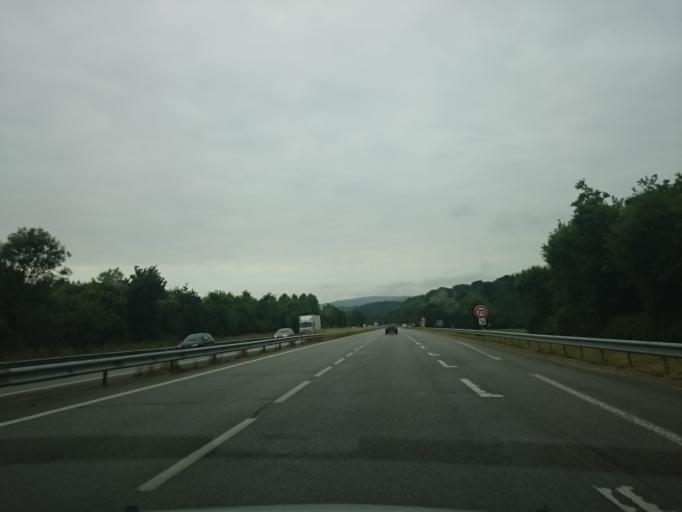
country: FR
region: Brittany
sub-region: Departement du Finistere
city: Dineault
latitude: 48.2600
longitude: -4.1139
